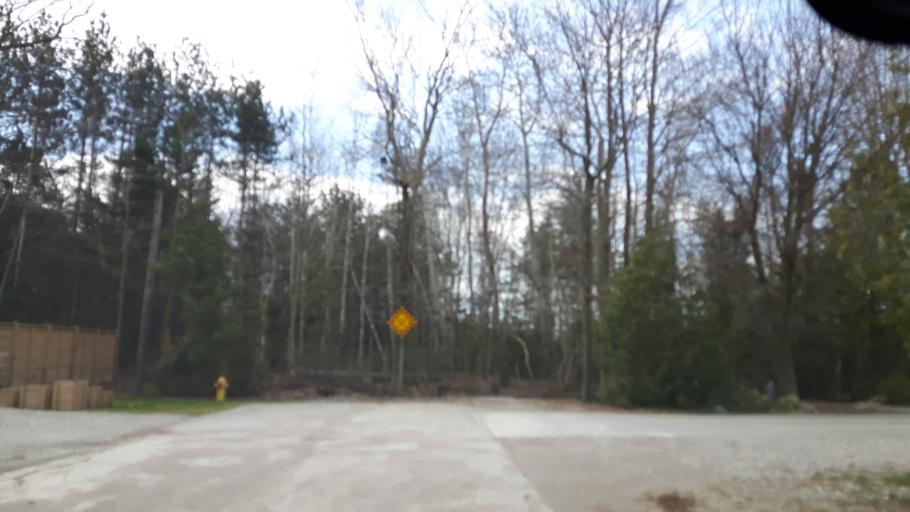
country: CA
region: Ontario
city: Bluewater
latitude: 43.5542
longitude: -81.6974
